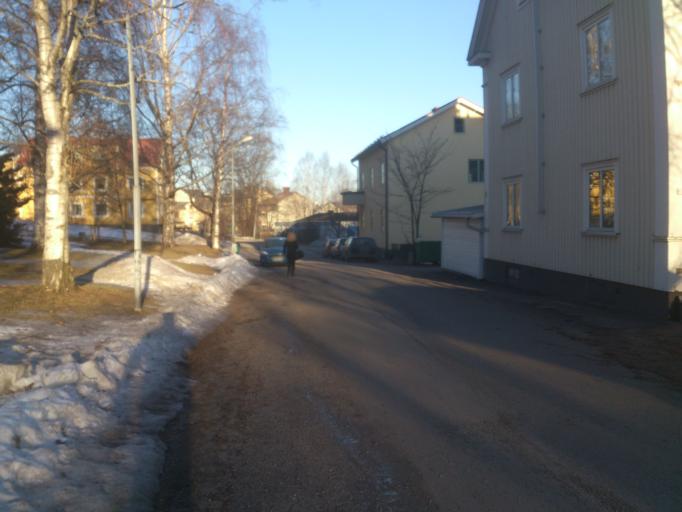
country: SE
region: Vaesternorrland
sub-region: Sundsvalls Kommun
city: Sundsvall
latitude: 62.3840
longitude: 17.3121
